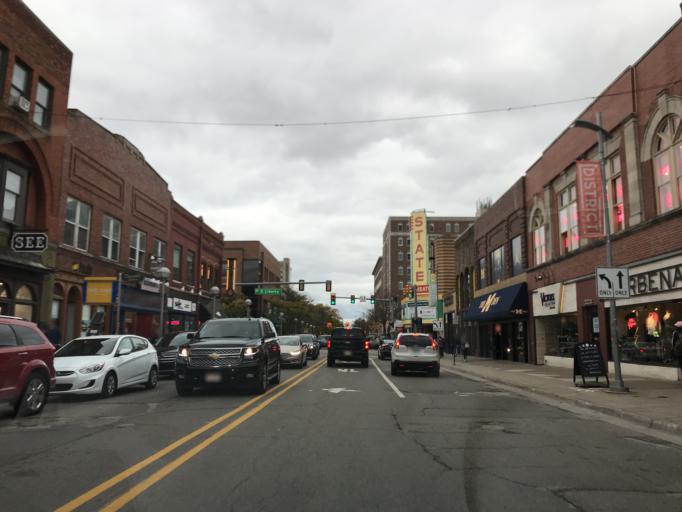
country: US
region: Michigan
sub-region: Washtenaw County
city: Ann Arbor
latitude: 42.2788
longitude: -83.7408
